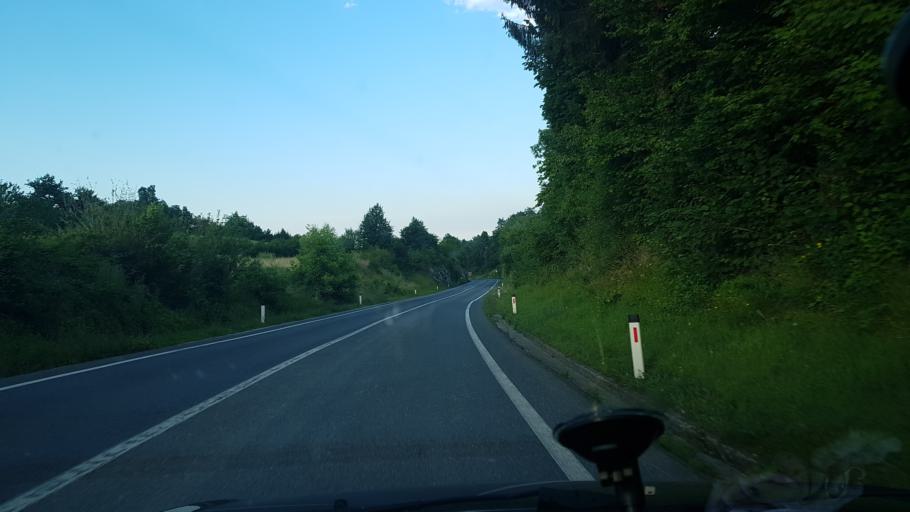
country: SI
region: Vrhnika
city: Vrhnika
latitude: 45.9564
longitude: 14.2702
